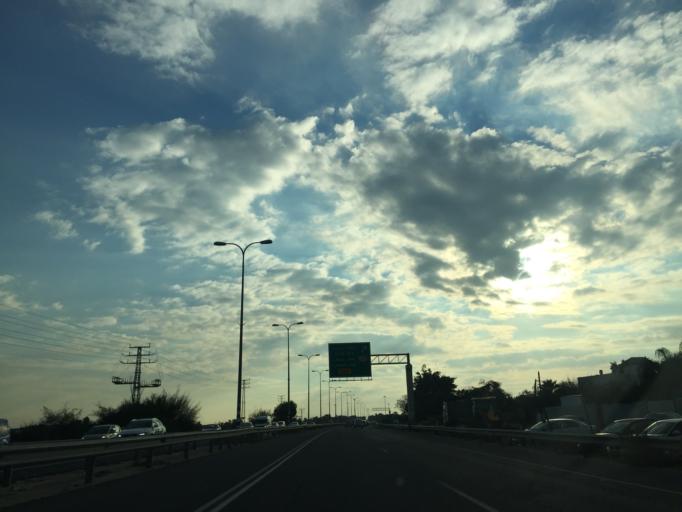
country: IL
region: Central District
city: Lod
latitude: 31.9303
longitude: 34.8897
